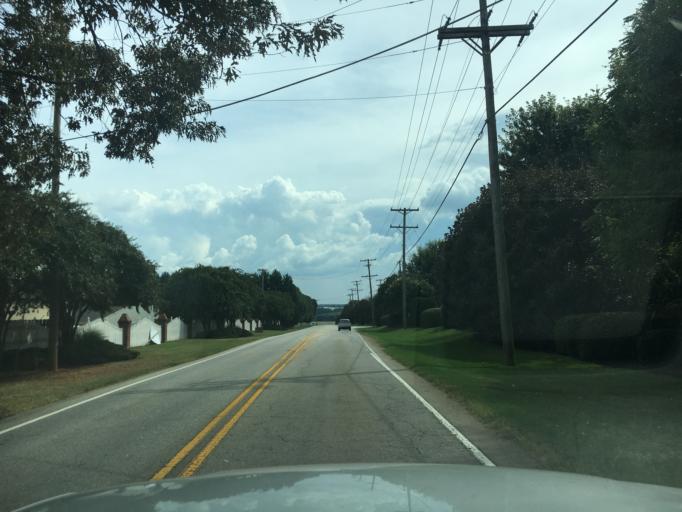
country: US
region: South Carolina
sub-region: Greenville County
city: Greer
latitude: 34.8854
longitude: -82.2417
